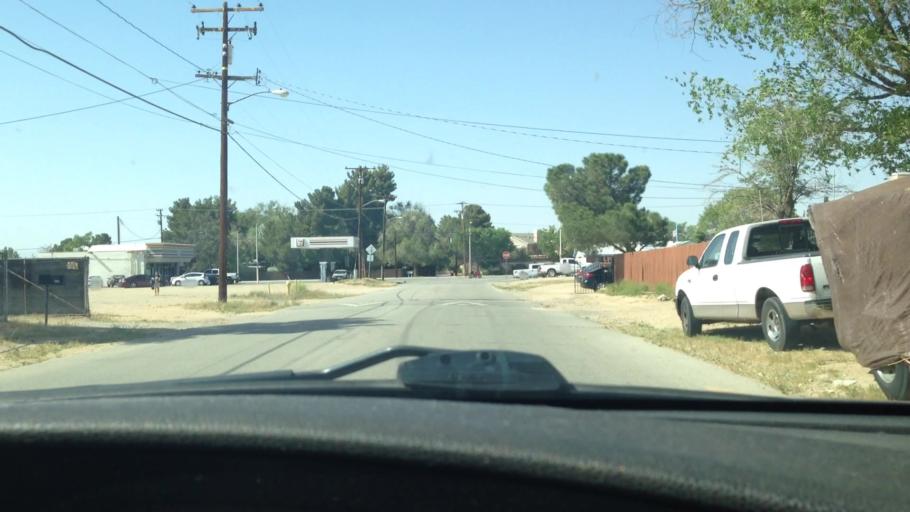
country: US
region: California
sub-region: Los Angeles County
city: Quartz Hill
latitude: 34.6589
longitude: -118.1879
